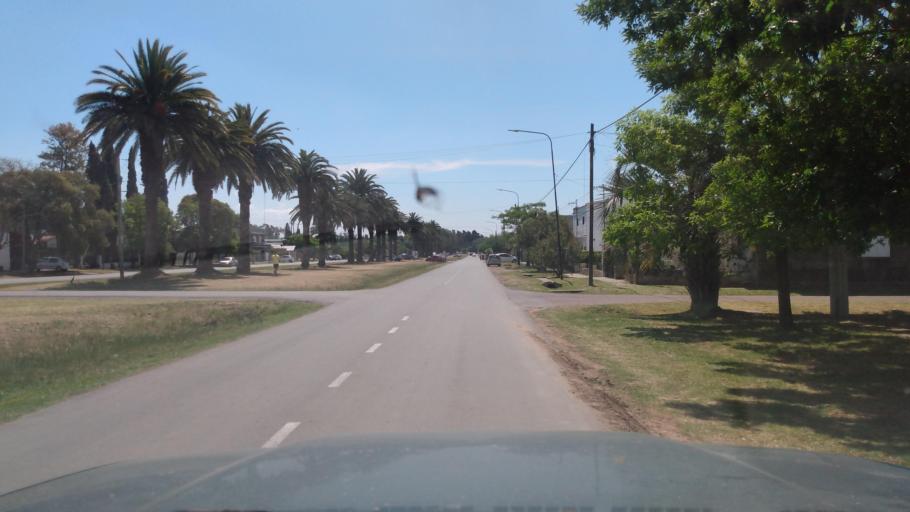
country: AR
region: Buenos Aires
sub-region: Partido de Lujan
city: Lujan
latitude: -34.5980
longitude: -59.1754
